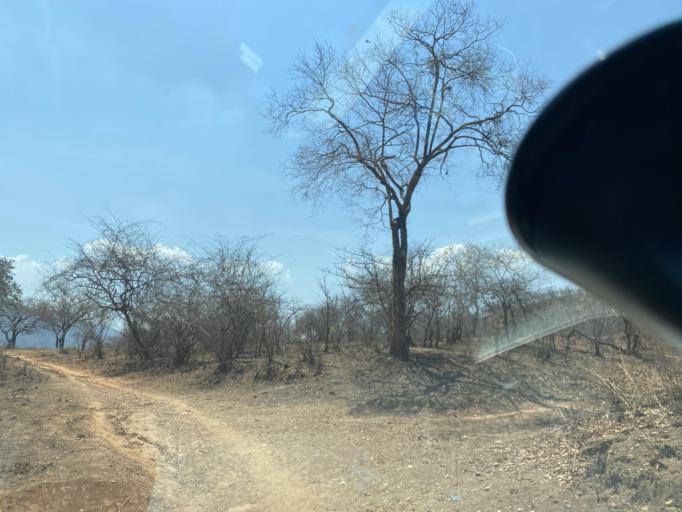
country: ZM
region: Lusaka
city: Kafue
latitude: -15.7801
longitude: 28.4602
